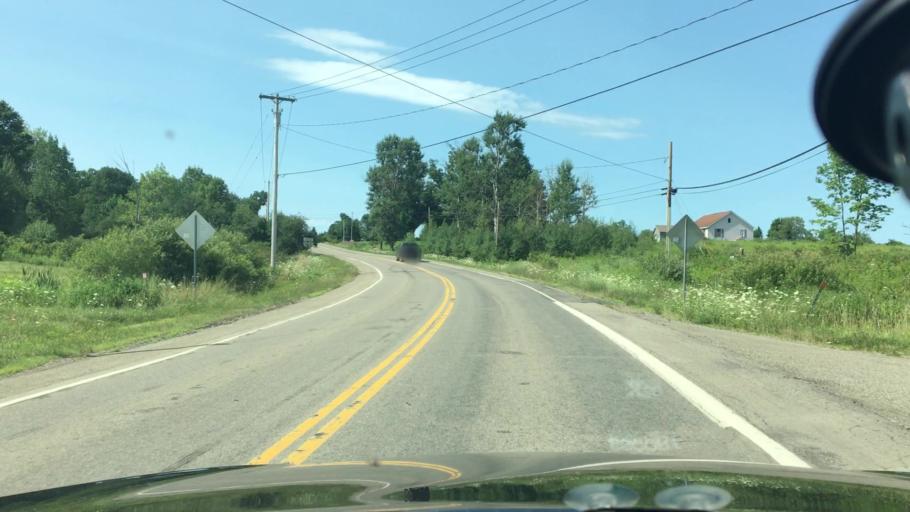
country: US
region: New York
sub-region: Chautauqua County
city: Mayville
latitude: 42.2603
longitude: -79.3480
